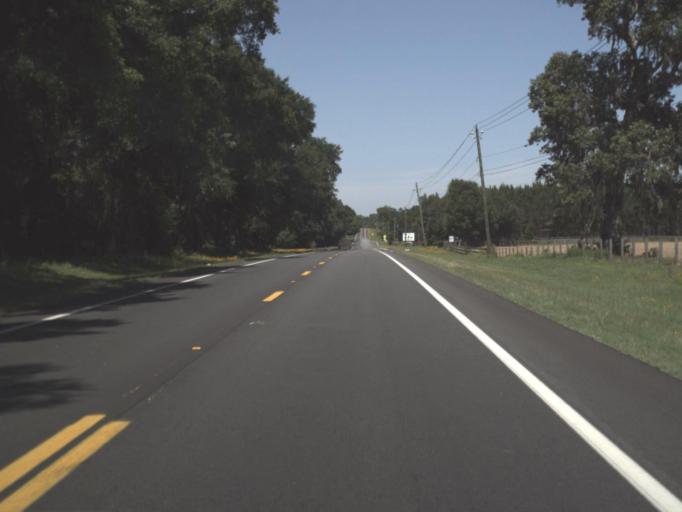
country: US
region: Florida
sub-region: Suwannee County
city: Wellborn
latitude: 30.1927
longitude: -82.7461
